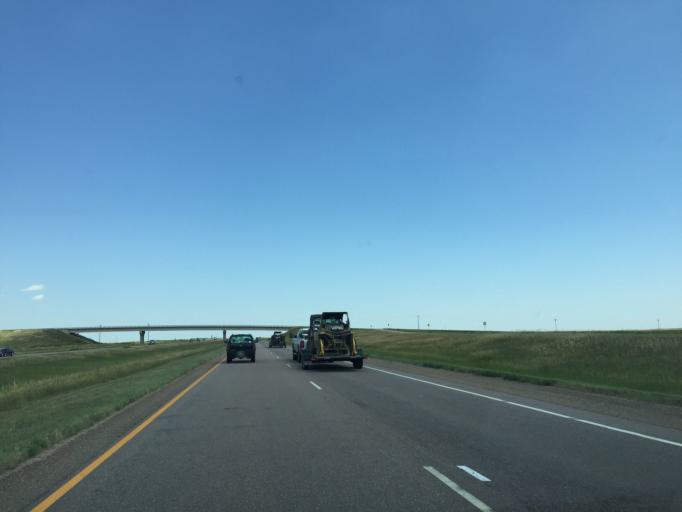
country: US
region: Colorado
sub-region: Lincoln County
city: Hugo
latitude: 39.2809
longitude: -103.3465
